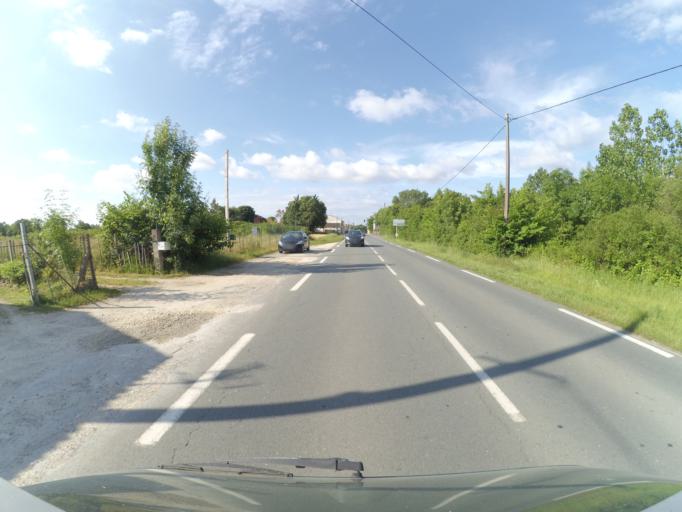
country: FR
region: Poitou-Charentes
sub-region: Departement de la Charente-Maritime
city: Le Gua
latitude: 45.7524
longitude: -0.9468
